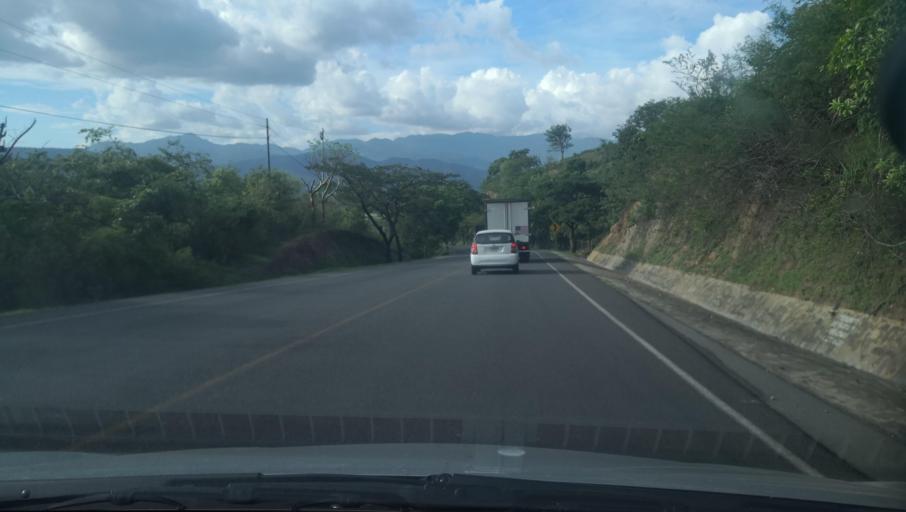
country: NI
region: Nueva Segovia
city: Ocotal
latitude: 13.5997
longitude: -86.4727
